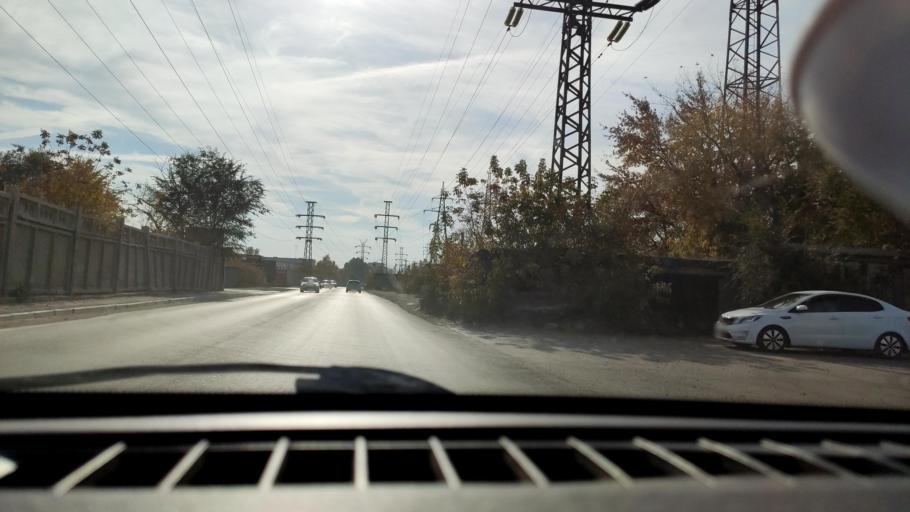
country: RU
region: Samara
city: Petra-Dubrava
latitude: 53.2460
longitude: 50.2923
